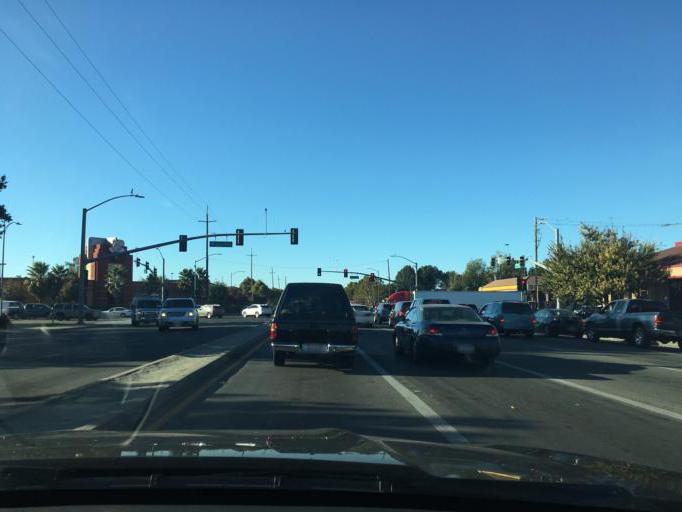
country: US
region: California
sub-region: Santa Clara County
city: Seven Trees
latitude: 37.3030
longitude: -121.8606
